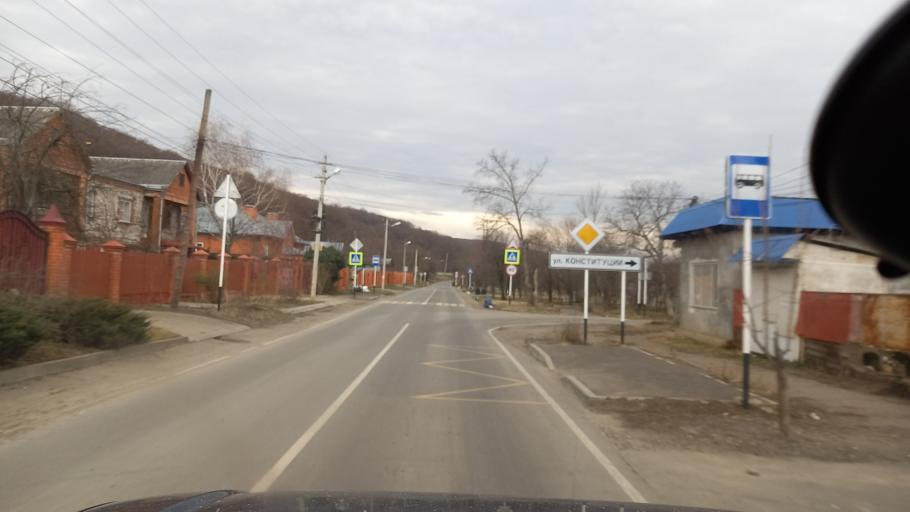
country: RU
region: Adygeya
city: Maykop
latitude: 44.5912
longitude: 40.0992
